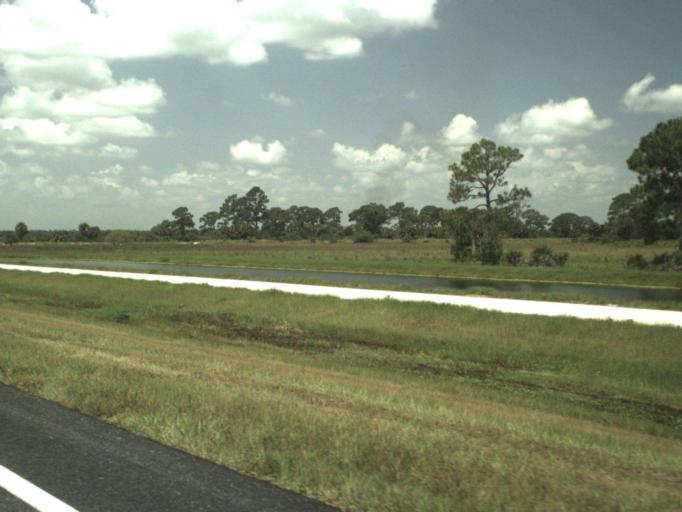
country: US
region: Florida
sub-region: Okeechobee County
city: Cypress Quarters
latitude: 27.3563
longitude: -80.6305
